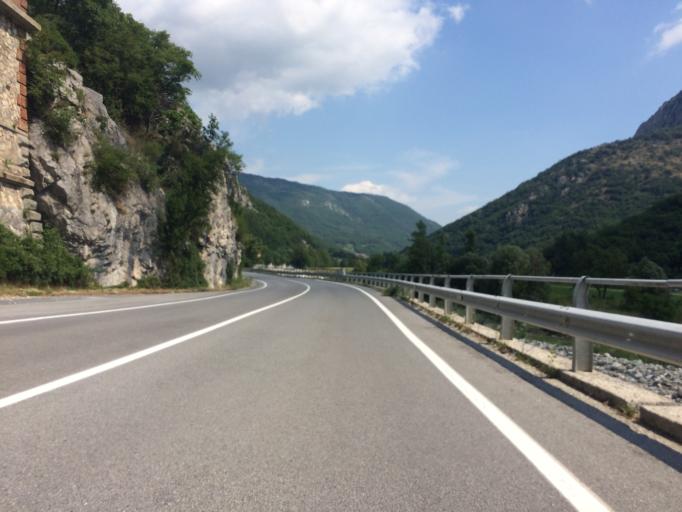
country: IT
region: Piedmont
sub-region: Provincia di Cuneo
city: Ormea
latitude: 44.1701
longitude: 7.9761
